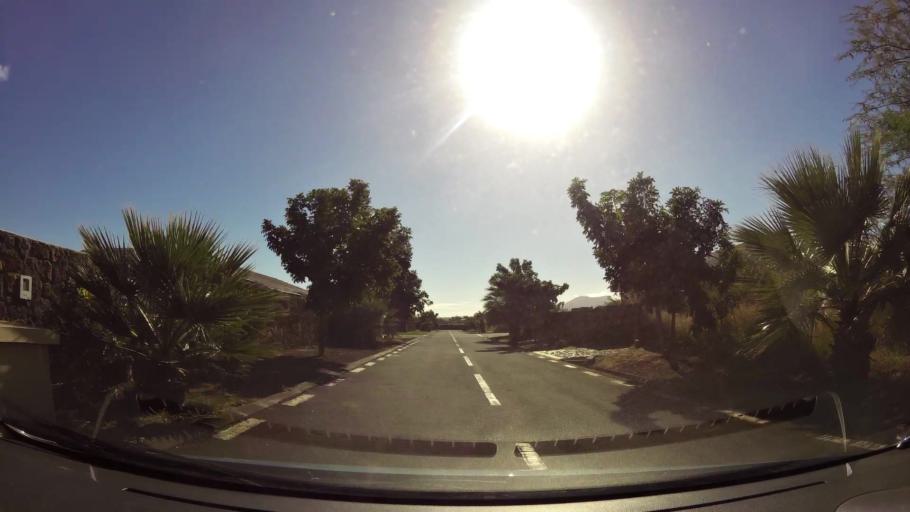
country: MU
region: Black River
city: Tamarin
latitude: -20.3372
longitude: 57.3661
